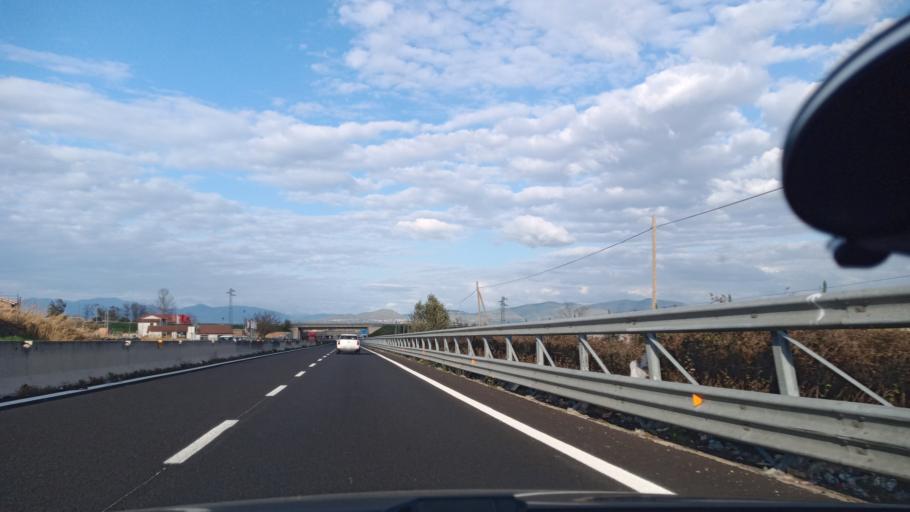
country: IT
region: Latium
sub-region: Citta metropolitana di Roma Capitale
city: Fiano Romano
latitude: 42.1454
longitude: 12.6170
